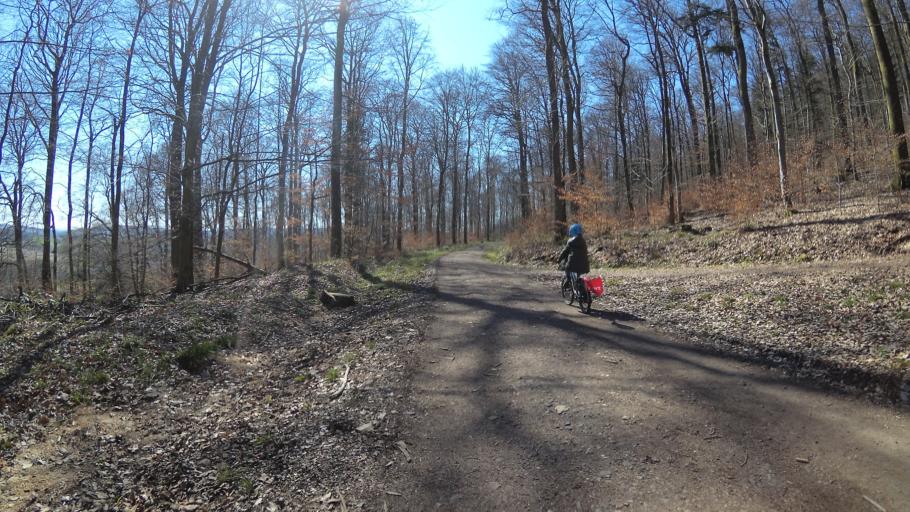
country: DE
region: Saarland
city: Sankt Wendel
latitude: 49.4388
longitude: 7.1794
